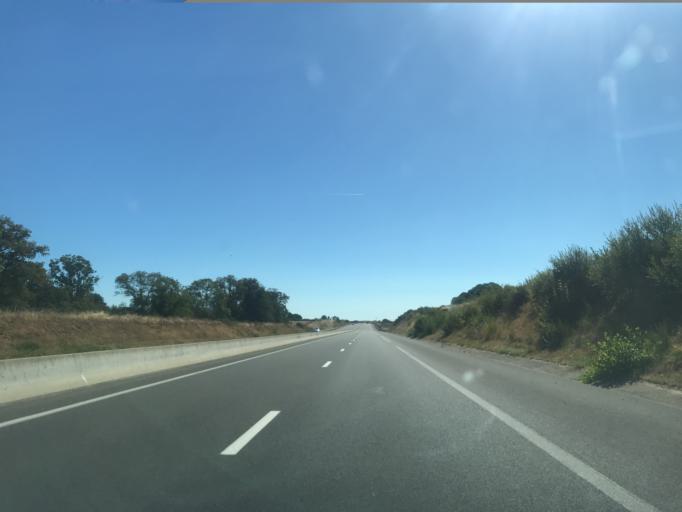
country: FR
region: Auvergne
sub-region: Departement de l'Allier
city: Quinssaines
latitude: 46.3165
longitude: 2.4886
